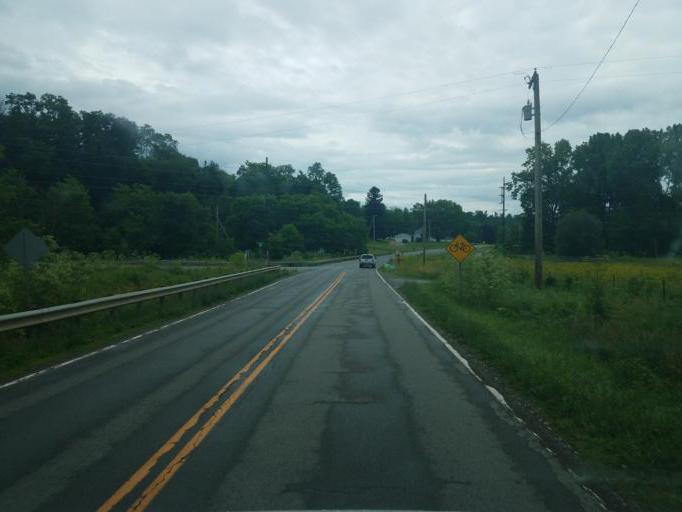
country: US
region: Ohio
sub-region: Richland County
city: Lexington
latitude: 40.7108
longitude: -82.5810
